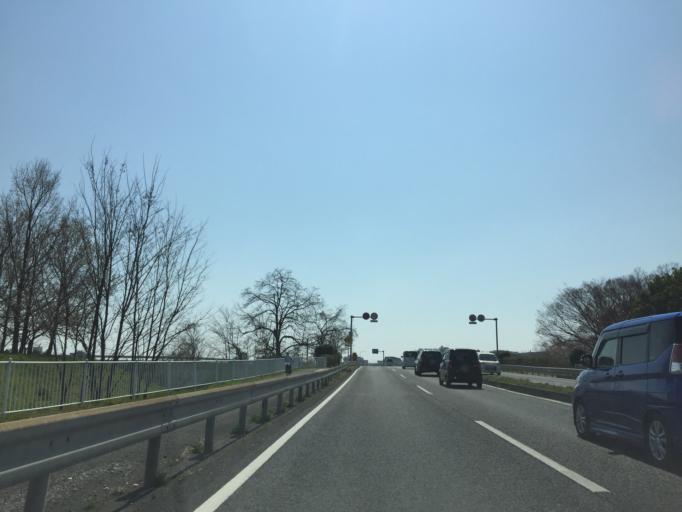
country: JP
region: Saitama
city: Oi
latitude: 35.8661
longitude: 139.5455
